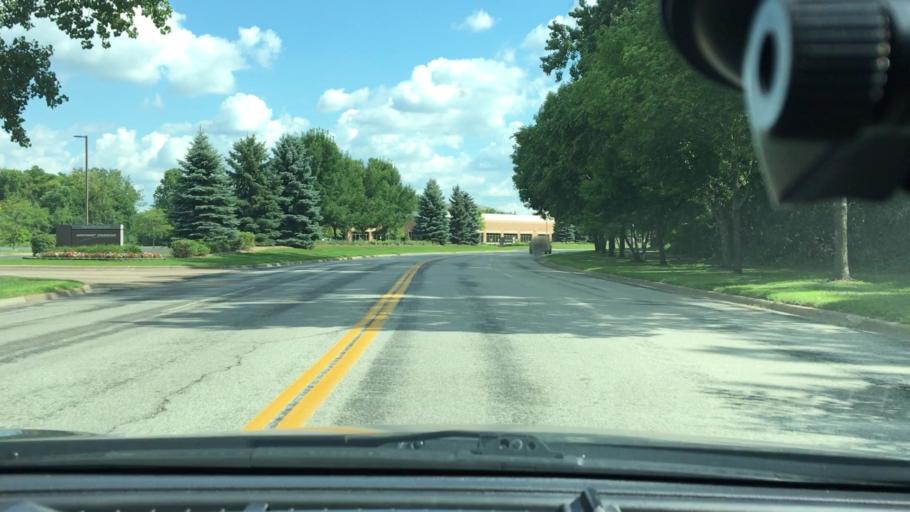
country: US
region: Minnesota
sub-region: Hennepin County
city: New Hope
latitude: 45.0410
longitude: -93.4057
